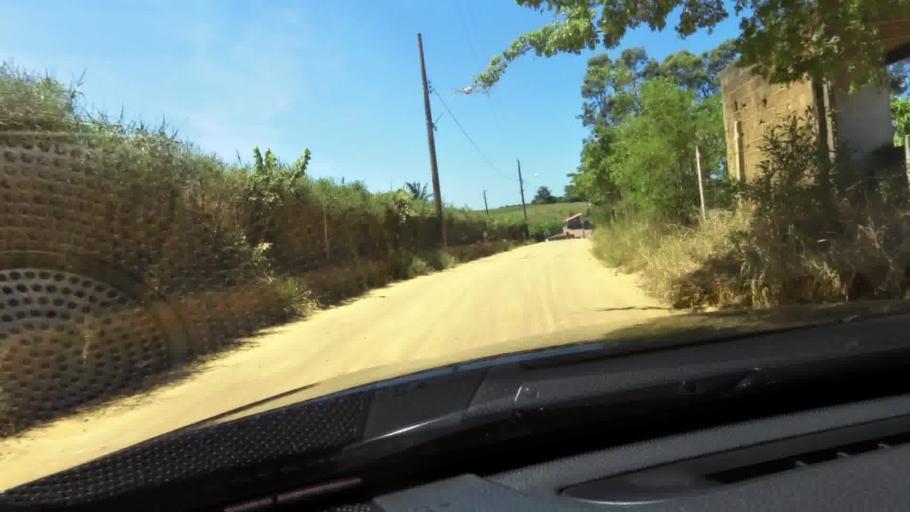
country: BR
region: Espirito Santo
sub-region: Guarapari
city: Guarapari
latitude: -20.6134
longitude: -40.4622
